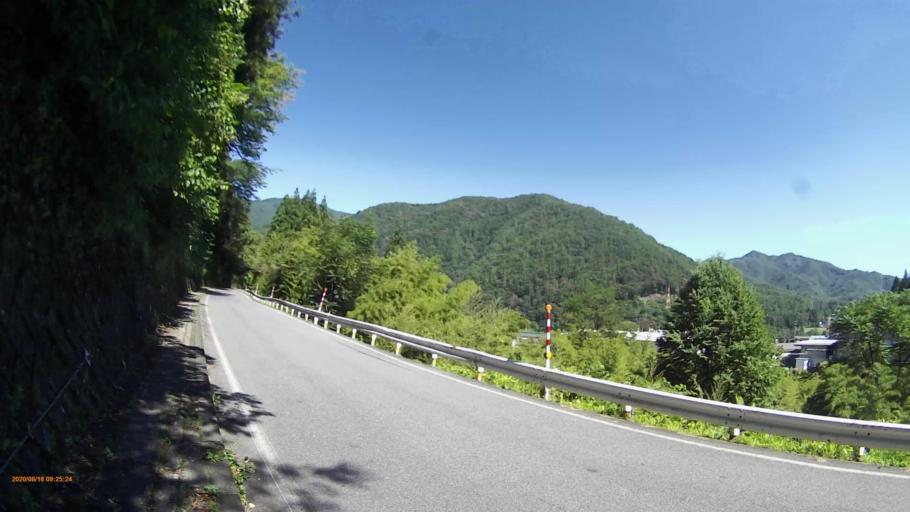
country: JP
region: Nagano
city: Iida
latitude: 35.6899
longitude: 137.6763
